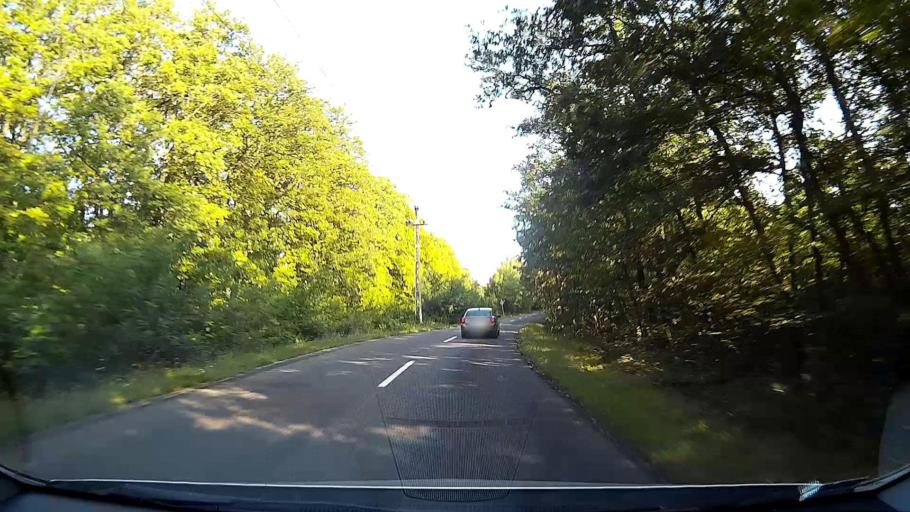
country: HU
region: Pest
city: Nagykovacsi
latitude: 47.7117
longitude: 19.0148
